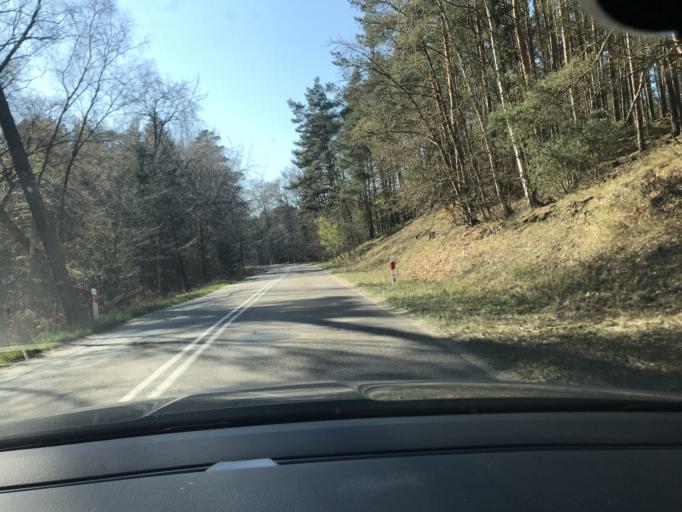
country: PL
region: Pomeranian Voivodeship
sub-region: Powiat nowodworski
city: Krynica Morska
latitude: 54.3641
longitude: 19.3669
